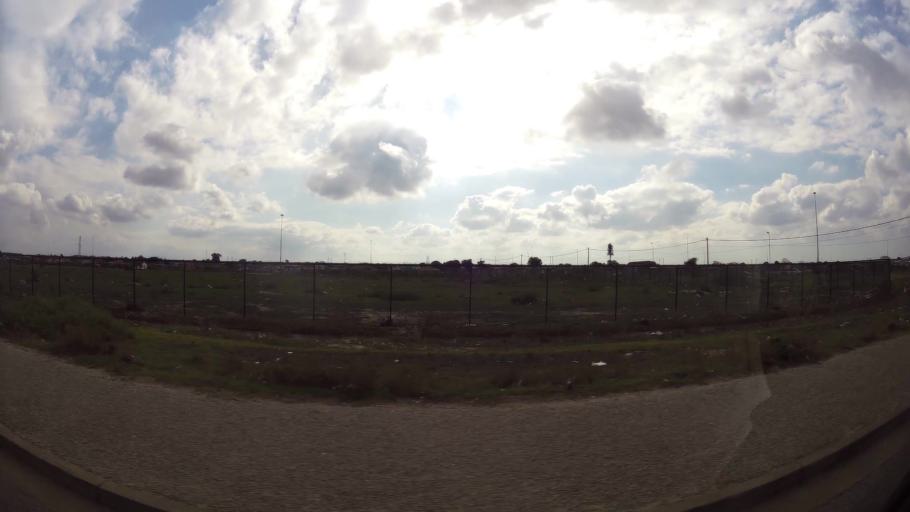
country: ZA
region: Eastern Cape
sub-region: Nelson Mandela Bay Metropolitan Municipality
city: Port Elizabeth
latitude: -33.8060
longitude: 25.5898
